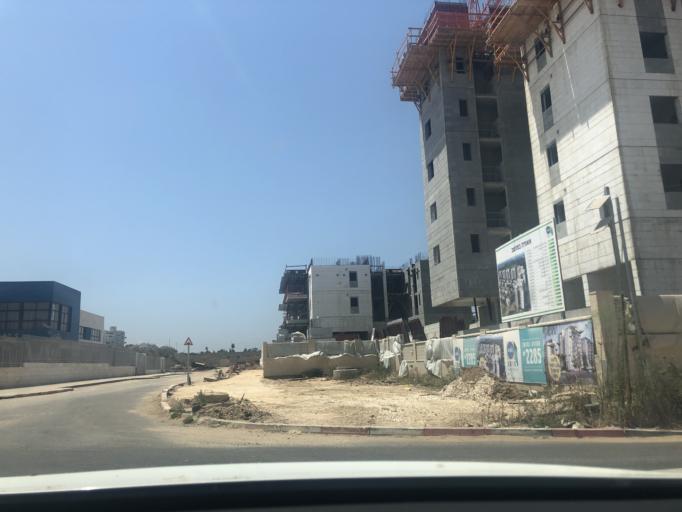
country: IL
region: Central District
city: Lod
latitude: 31.9346
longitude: 34.8967
